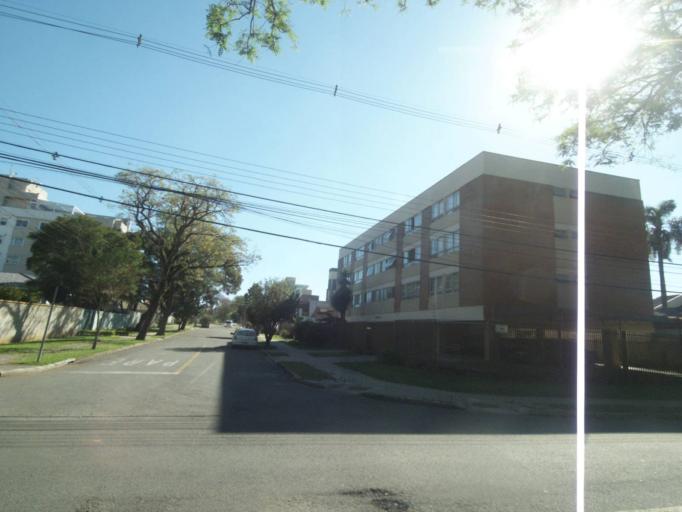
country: BR
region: Parana
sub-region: Curitiba
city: Curitiba
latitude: -25.3928
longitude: -49.2330
